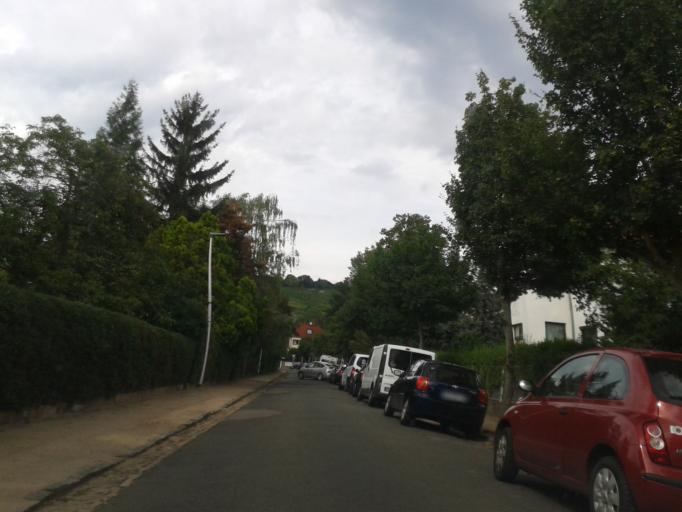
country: DE
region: Saxony
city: Radebeul
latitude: 51.1073
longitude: 13.6576
